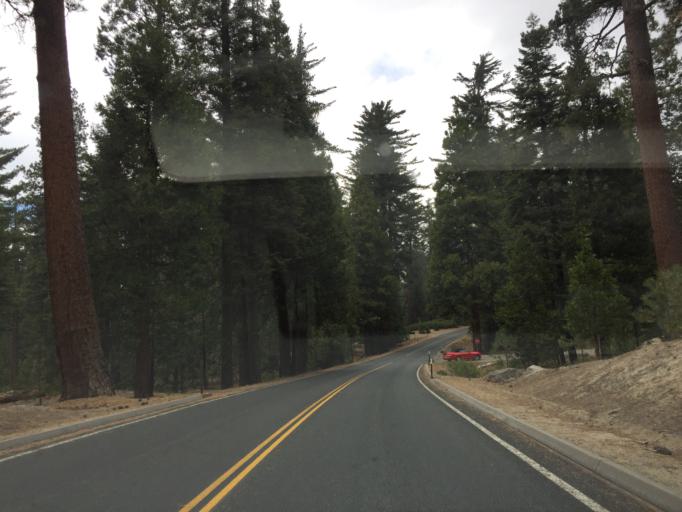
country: US
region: California
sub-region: Fresno County
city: Squaw Valley
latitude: 36.7359
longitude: -118.9638
